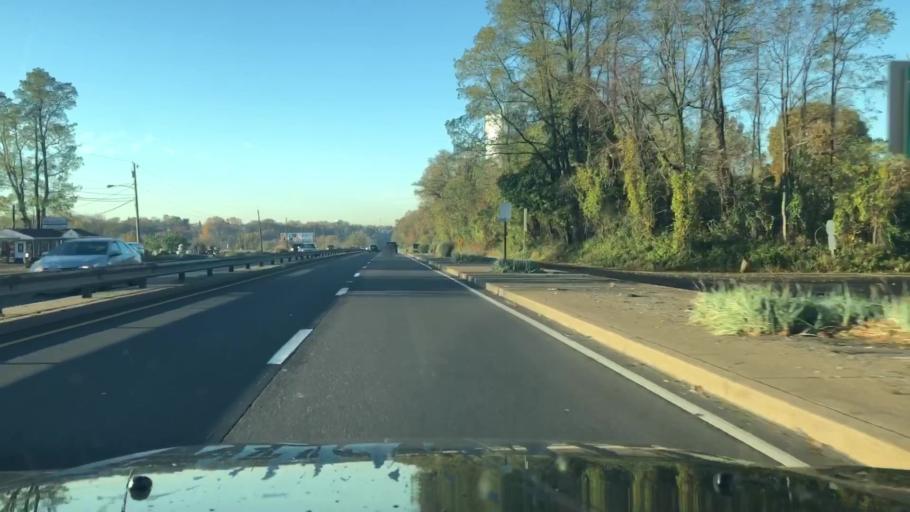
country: US
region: Pennsylvania
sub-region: Bucks County
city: Penndel
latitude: 40.1555
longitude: -74.9431
